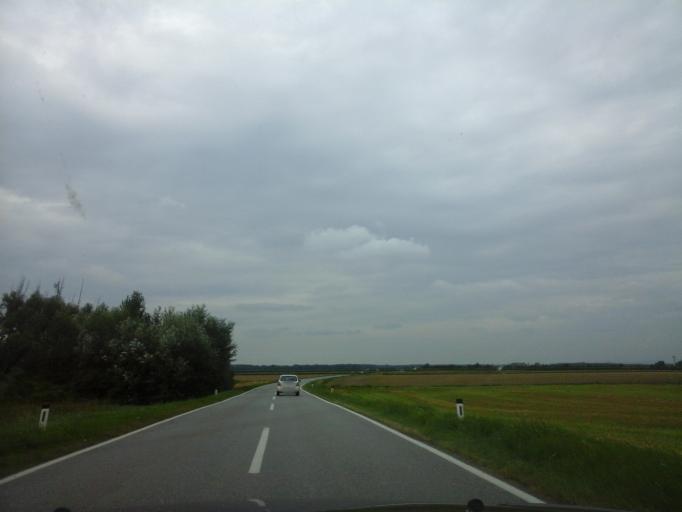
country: AT
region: Lower Austria
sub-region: Politischer Bezirk Ganserndorf
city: Orth an der Donau
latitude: 48.1595
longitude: 16.7438
